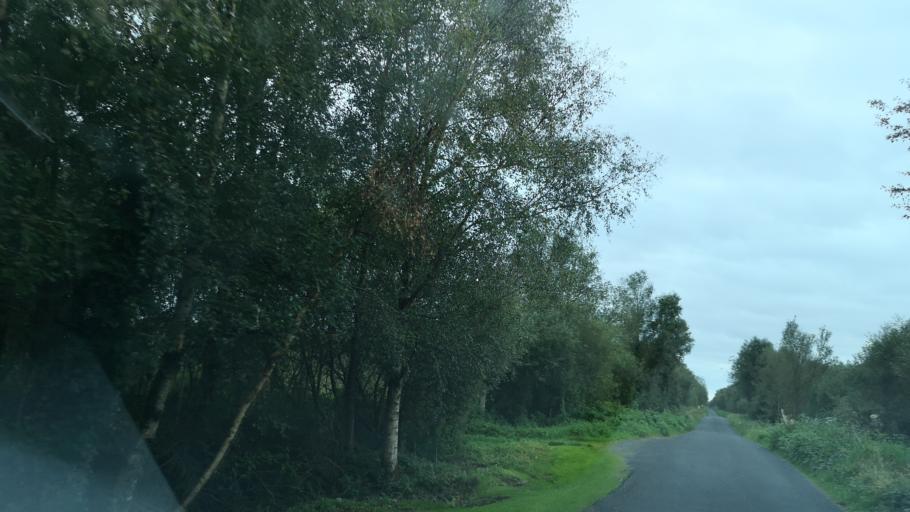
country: IE
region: Leinster
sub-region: Uibh Fhaili
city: Ferbane
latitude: 53.2008
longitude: -7.7249
